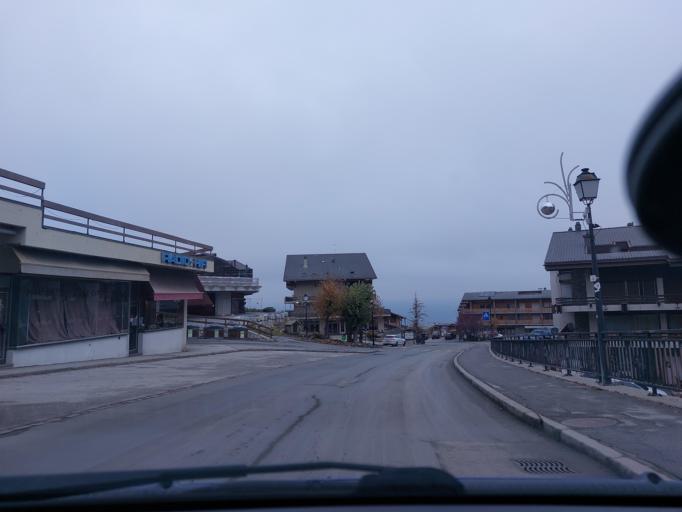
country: CH
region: Valais
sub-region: Conthey District
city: Basse-Nendaz
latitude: 46.1818
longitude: 7.2947
